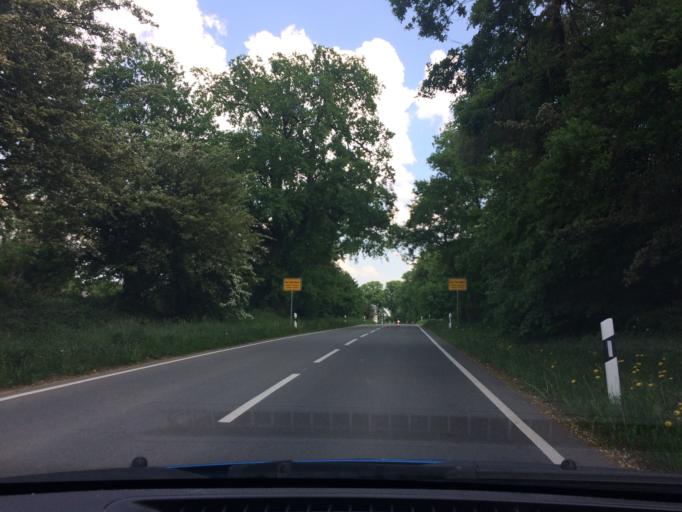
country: DE
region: Lower Saxony
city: Tosterglope
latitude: 53.1966
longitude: 10.7923
